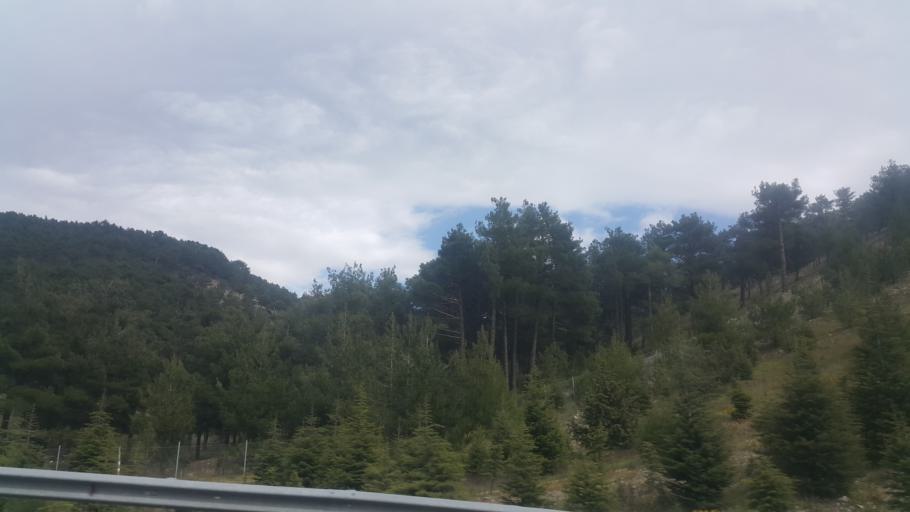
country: TR
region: Adana
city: Pozanti
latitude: 37.4338
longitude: 34.8821
